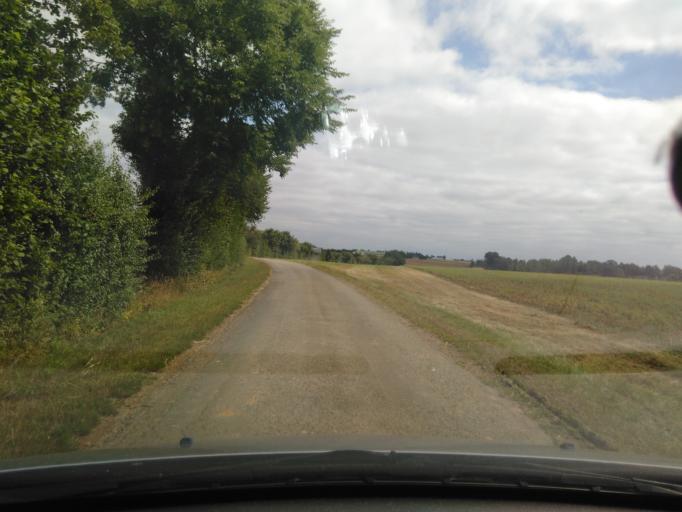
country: FR
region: Pays de la Loire
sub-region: Departement de la Vendee
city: Sainte-Gemme-la-Plaine
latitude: 46.5261
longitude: -1.0959
